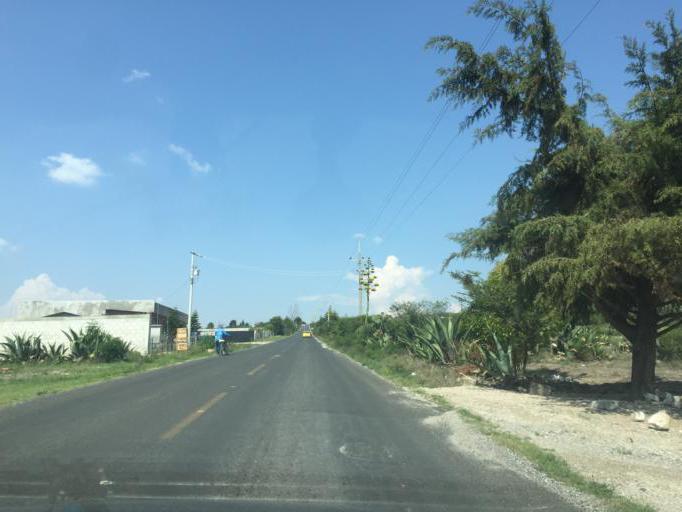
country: MX
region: Hidalgo
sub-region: Cardonal
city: Pozuelos
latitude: 20.6145
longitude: -99.0733
